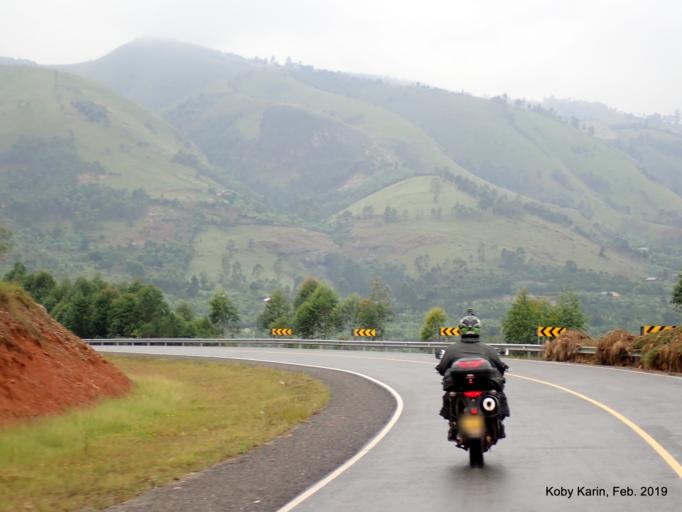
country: UG
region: Western Region
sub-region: Mitoma District
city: Mitoma
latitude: -0.7046
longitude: 30.1659
